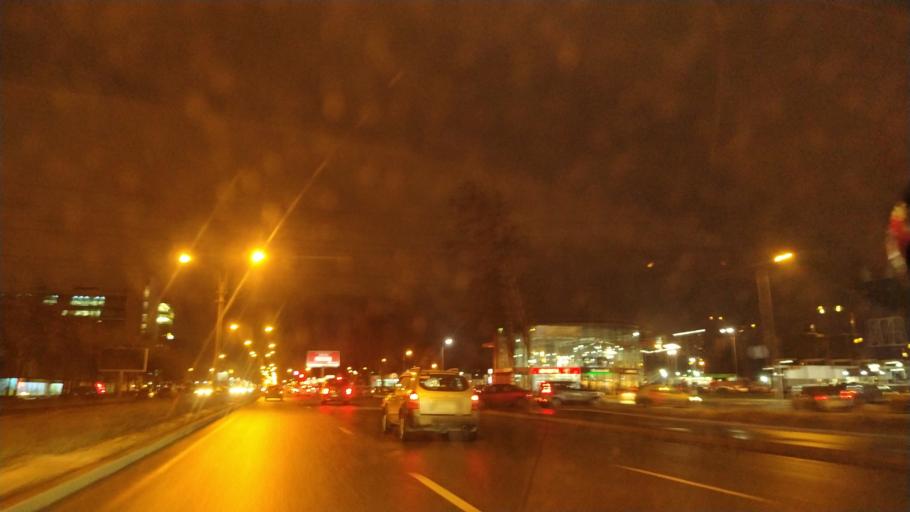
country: RU
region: St.-Petersburg
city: Kupchino
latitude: 59.8329
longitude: 30.3405
